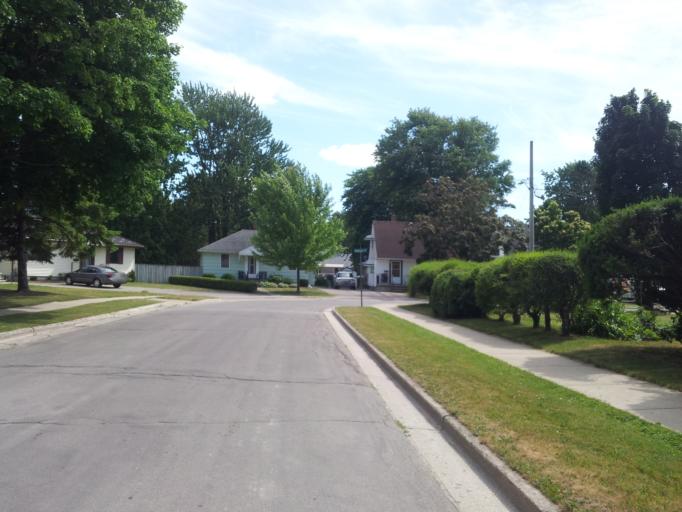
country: CA
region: Ontario
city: Stratford
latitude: 43.3723
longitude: -80.9611
